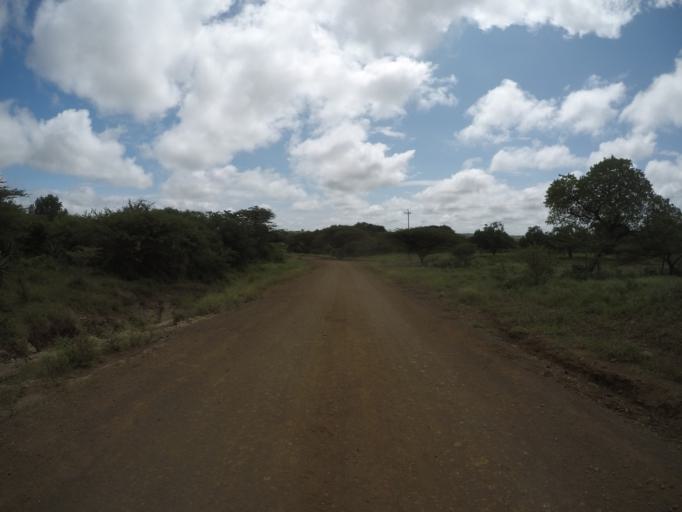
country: ZA
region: KwaZulu-Natal
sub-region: uThungulu District Municipality
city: Empangeni
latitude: -28.5725
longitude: 31.8372
